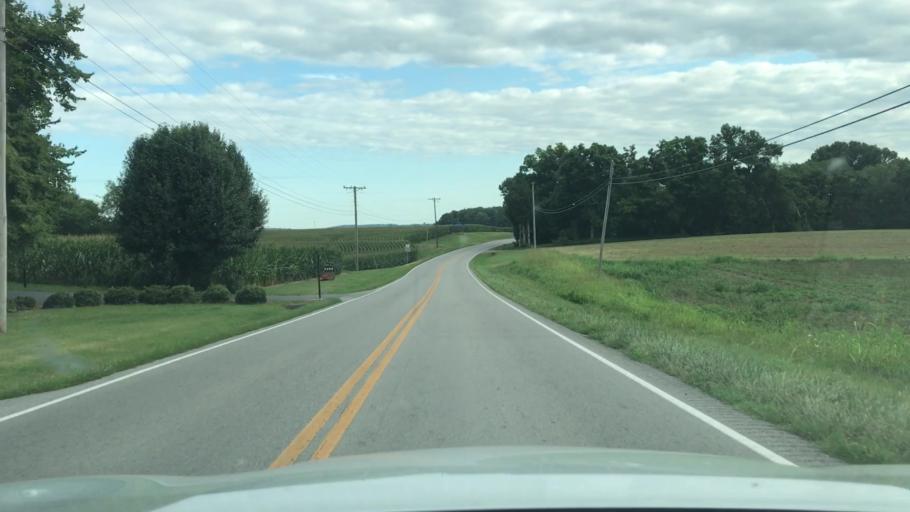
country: US
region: Kentucky
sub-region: Todd County
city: Elkton
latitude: 36.7883
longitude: -87.1641
